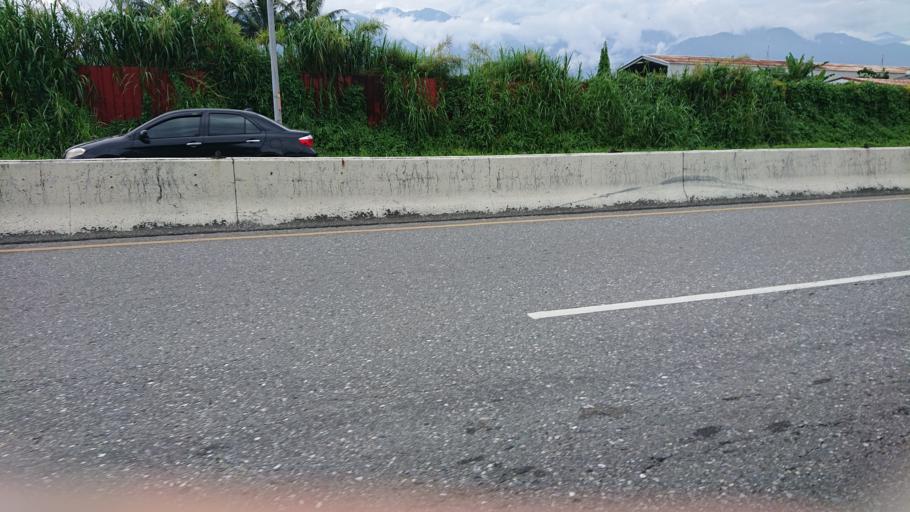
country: TW
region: Taiwan
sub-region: Hualien
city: Hualian
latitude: 23.9430
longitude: 121.5958
